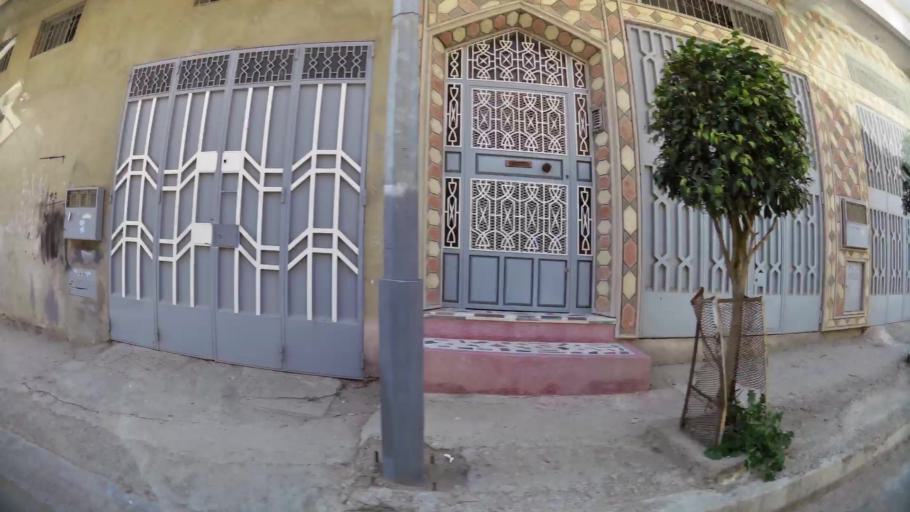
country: MA
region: Tanger-Tetouan
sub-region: Tanger-Assilah
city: Tangier
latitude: 35.7327
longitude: -5.8084
